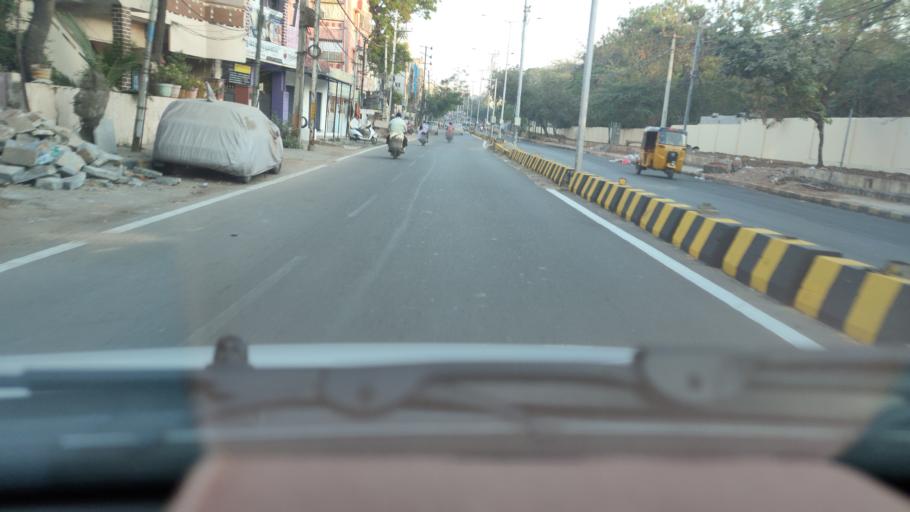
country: IN
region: Telangana
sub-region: Rangareddi
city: Gaddi Annaram
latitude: 17.3880
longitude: 78.5165
